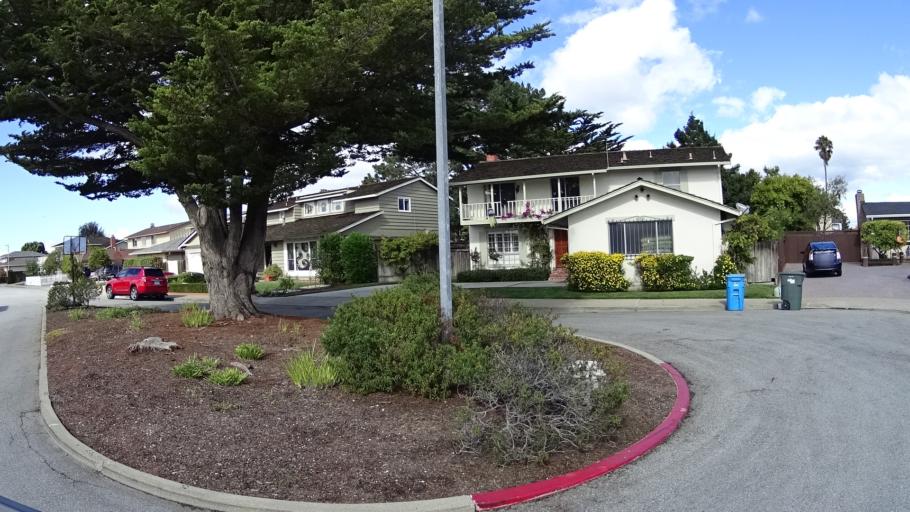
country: US
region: California
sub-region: San Mateo County
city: Foster City
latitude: 37.5678
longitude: -122.2593
